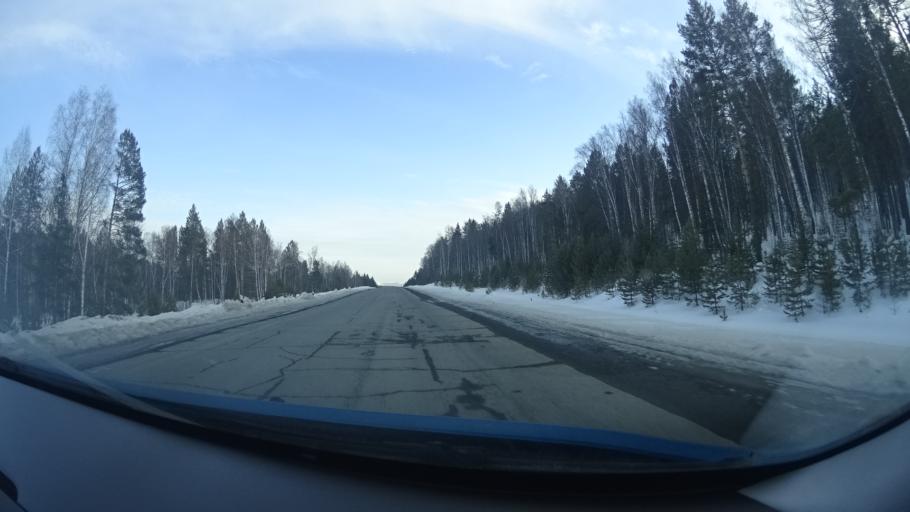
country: RU
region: Bashkortostan
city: Lomovka
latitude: 53.4805
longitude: 58.3146
